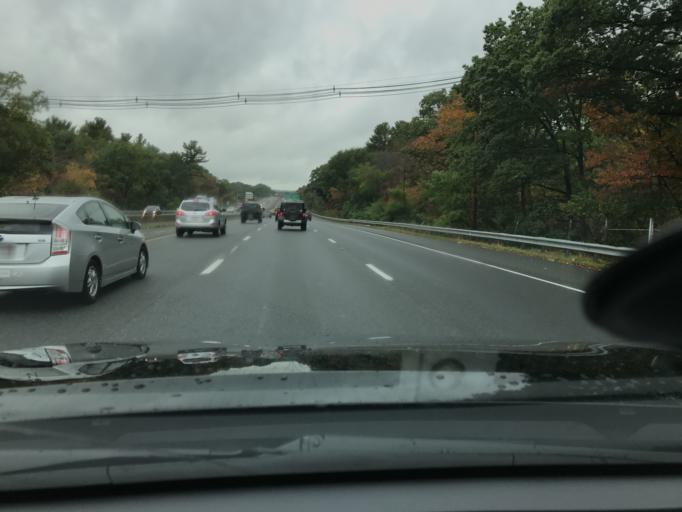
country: US
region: Massachusetts
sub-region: Essex County
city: Lynnfield
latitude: 42.5152
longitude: -71.0190
